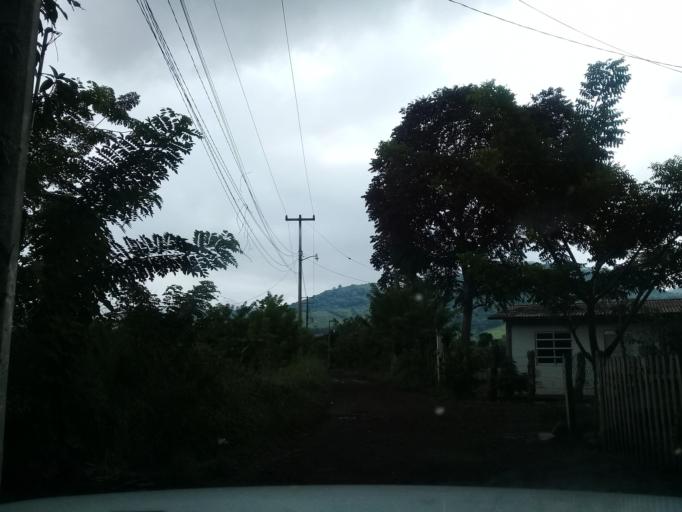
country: MX
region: Veracruz
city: Comoapan
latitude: 18.4024
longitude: -95.1729
